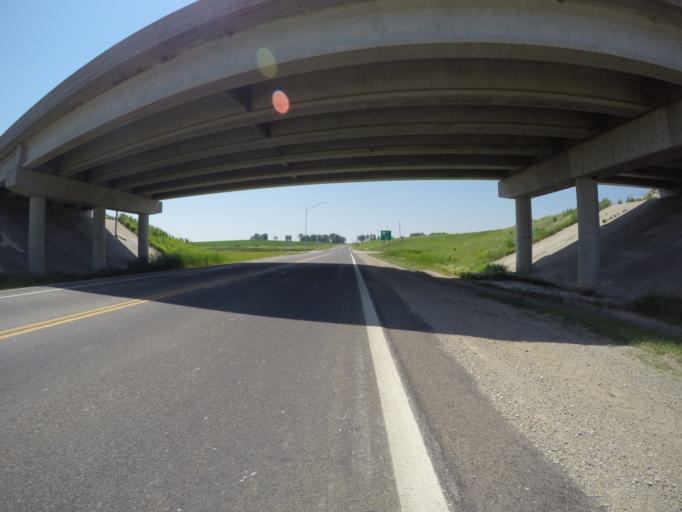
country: US
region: Kansas
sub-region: Doniphan County
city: Highland
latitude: 39.8400
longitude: -95.2652
